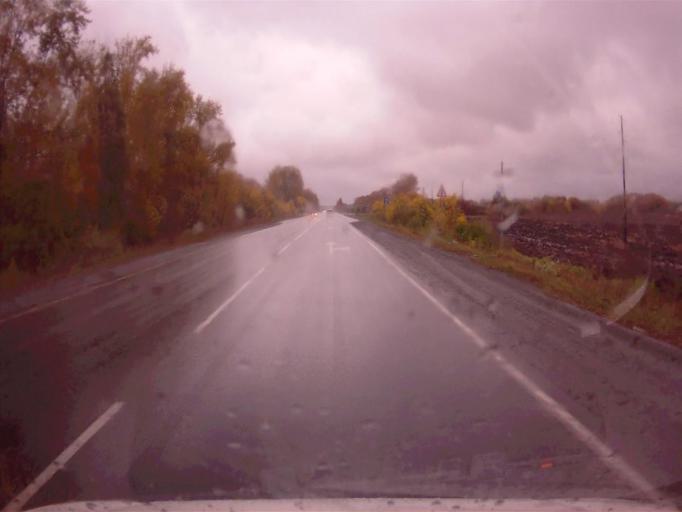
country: RU
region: Chelyabinsk
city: Argayash
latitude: 55.4329
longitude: 60.9841
